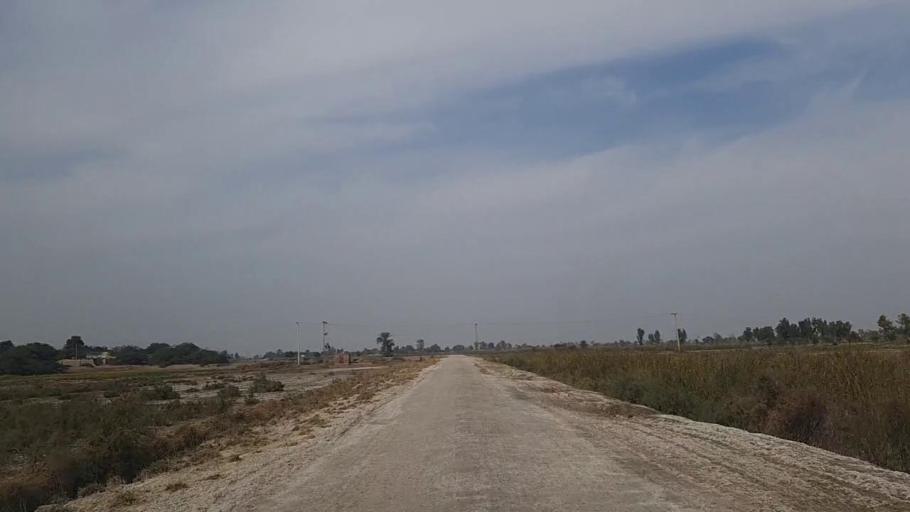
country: PK
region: Sindh
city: Daur
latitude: 26.4809
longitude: 68.4055
